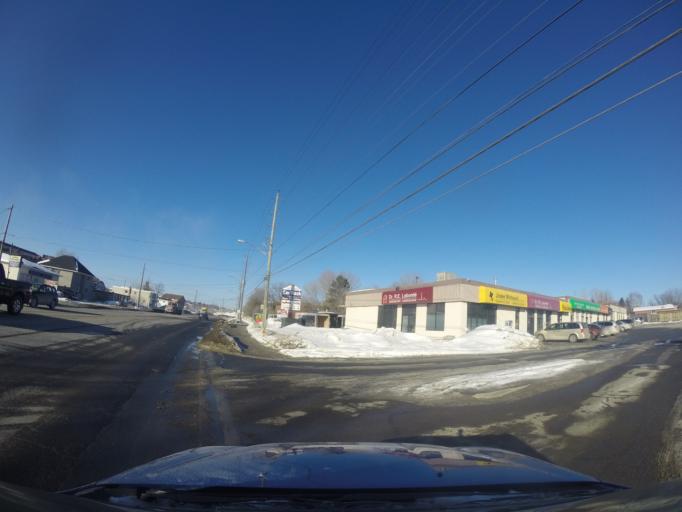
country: CA
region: Ontario
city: Greater Sudbury
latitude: 46.4619
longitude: -81.0004
